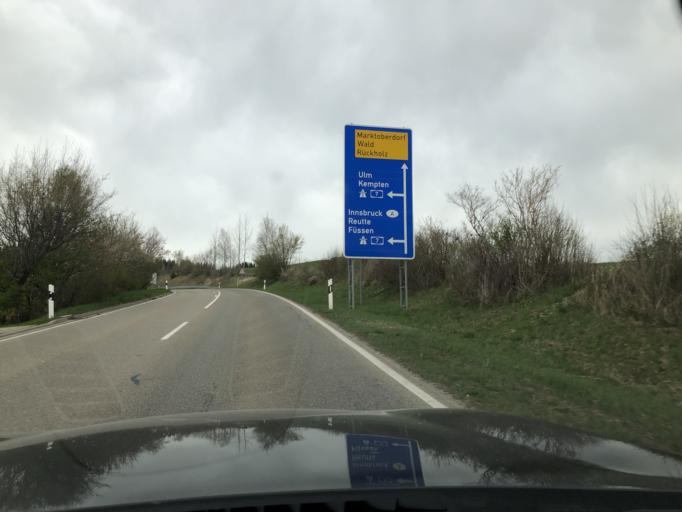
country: DE
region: Bavaria
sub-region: Swabia
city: Nesselwang
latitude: 47.6383
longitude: 10.5278
